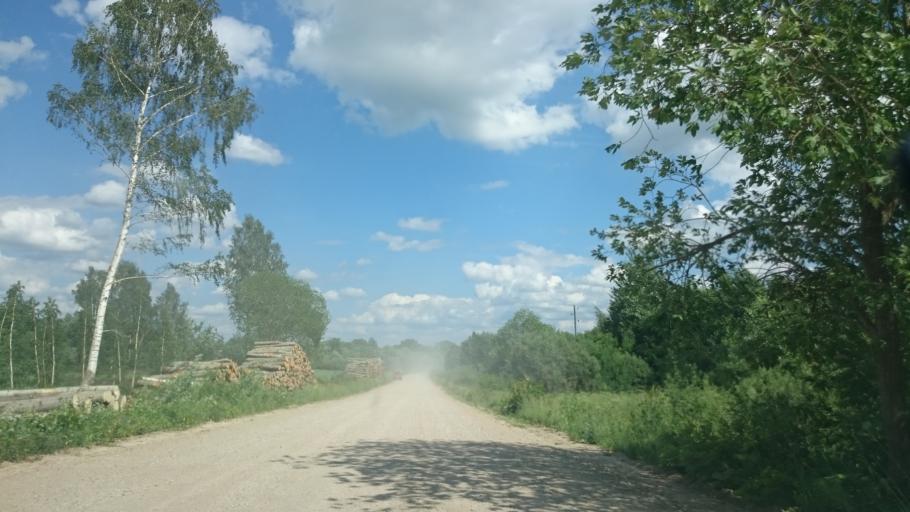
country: LV
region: Cibla
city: Cibla
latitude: 56.5608
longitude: 27.8456
